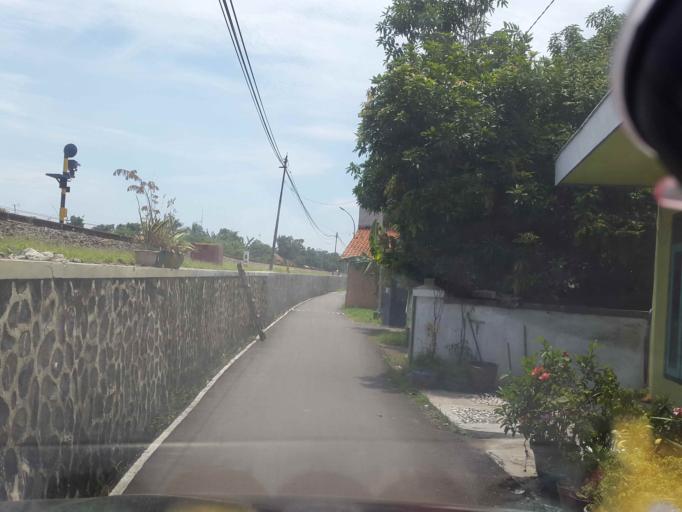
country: ID
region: Central Java
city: Tegal
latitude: -6.8598
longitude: 109.1484
